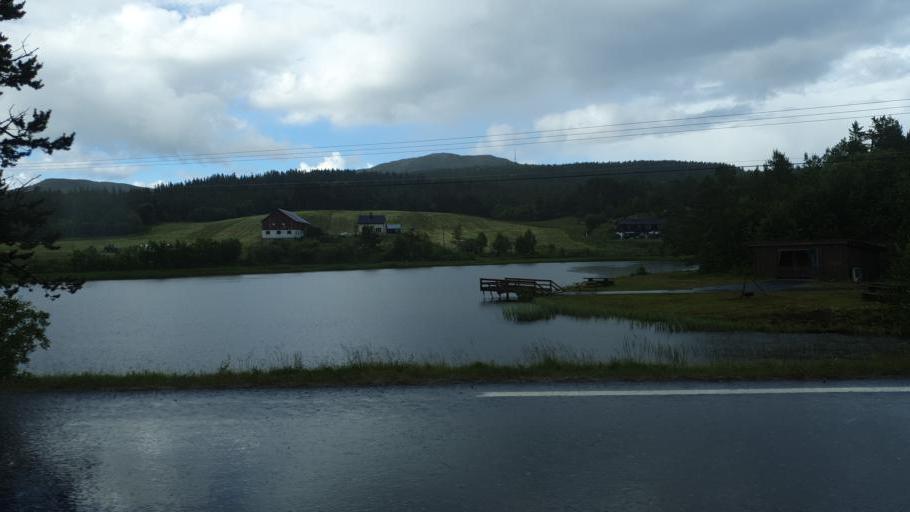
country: NO
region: Oppland
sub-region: Vaga
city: Vagamo
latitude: 61.8112
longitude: 9.0087
